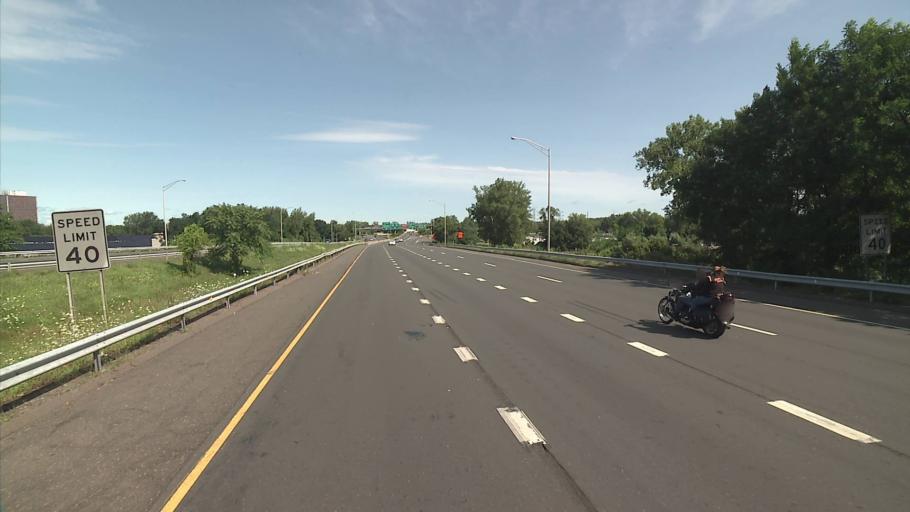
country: US
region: Connecticut
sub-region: Hartford County
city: Hartford
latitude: 41.7597
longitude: -72.6530
